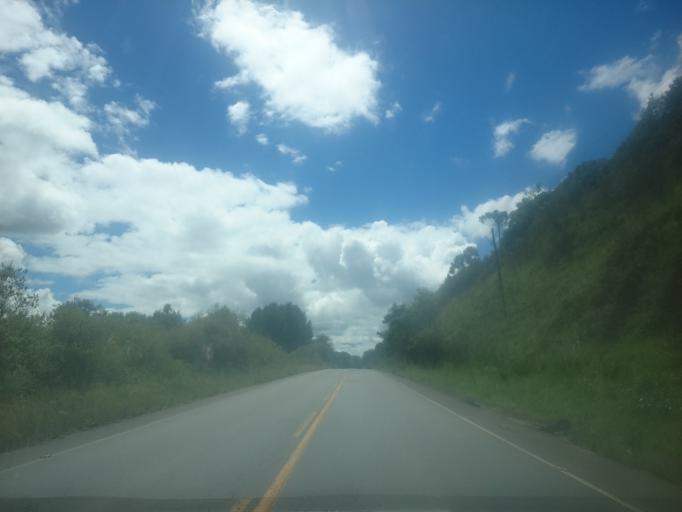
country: BR
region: Santa Catarina
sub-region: Otacilio Costa
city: Otacilio Costa
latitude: -27.6480
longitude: -50.1911
